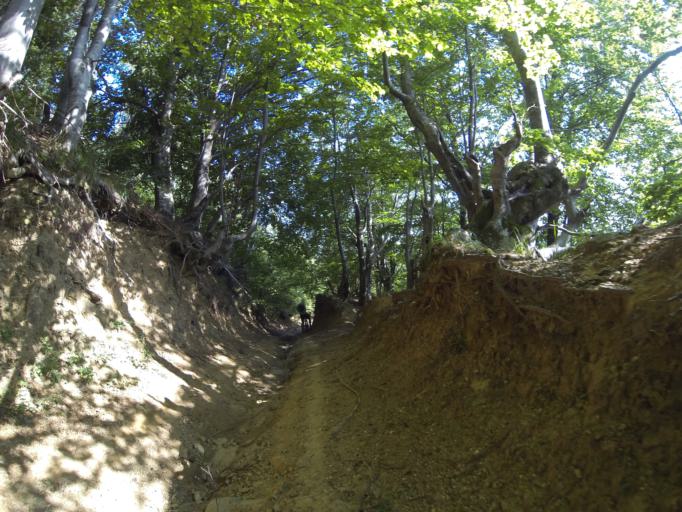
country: RO
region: Valcea
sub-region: Comuna Vaideeni
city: Vaideeni
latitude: 45.2133
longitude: 23.9723
